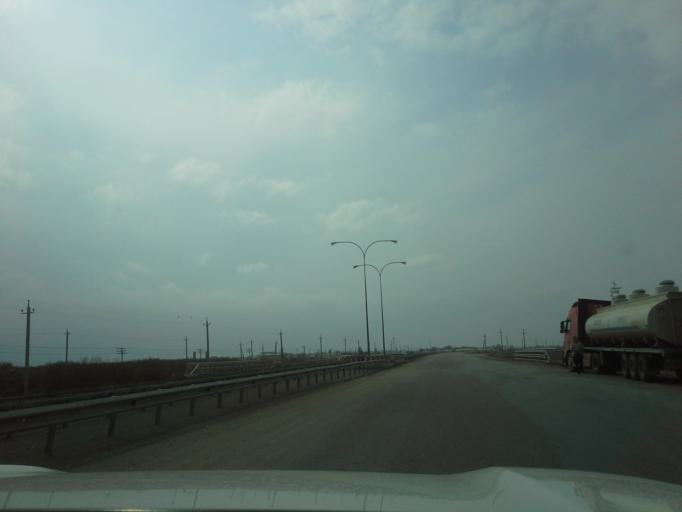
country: IR
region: Razavi Khorasan
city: Kalat-e Naderi
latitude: 37.2043
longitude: 60.0456
